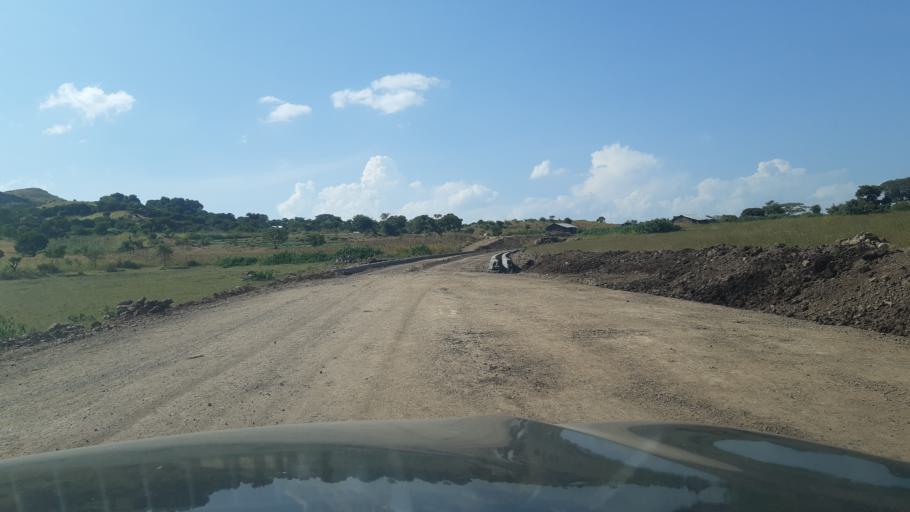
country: ET
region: Amhara
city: Dabat
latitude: 13.1592
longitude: 37.6087
